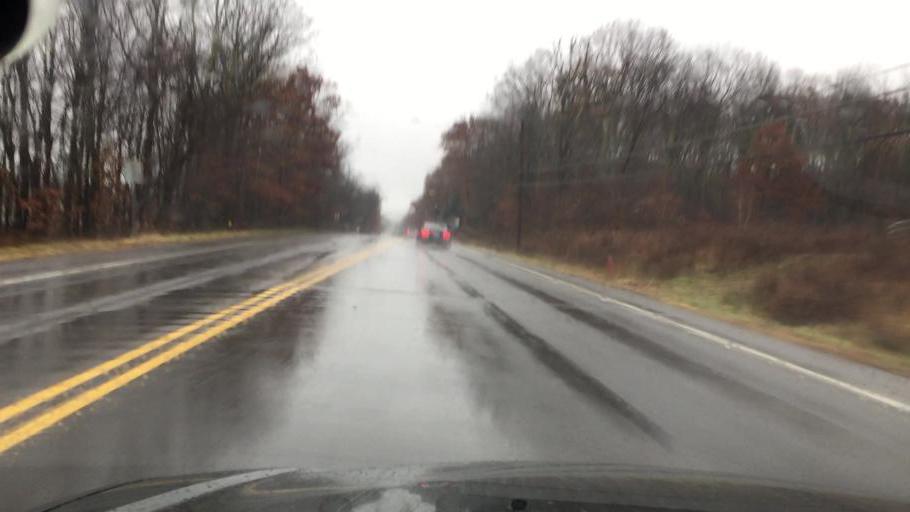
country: US
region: Pennsylvania
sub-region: Luzerne County
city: Mountain Top
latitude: 41.1019
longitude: -75.9270
